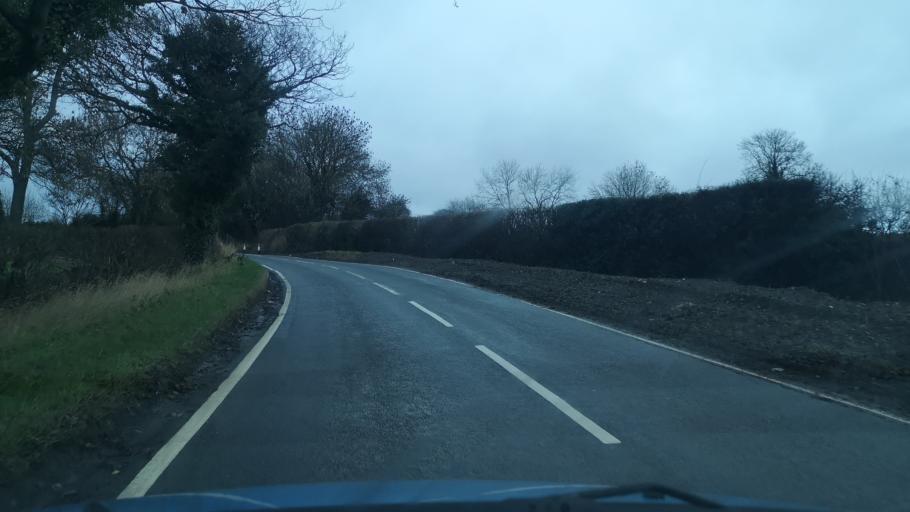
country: GB
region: England
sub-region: City and Borough of Wakefield
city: Ryhill
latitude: 53.6382
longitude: -1.4021
